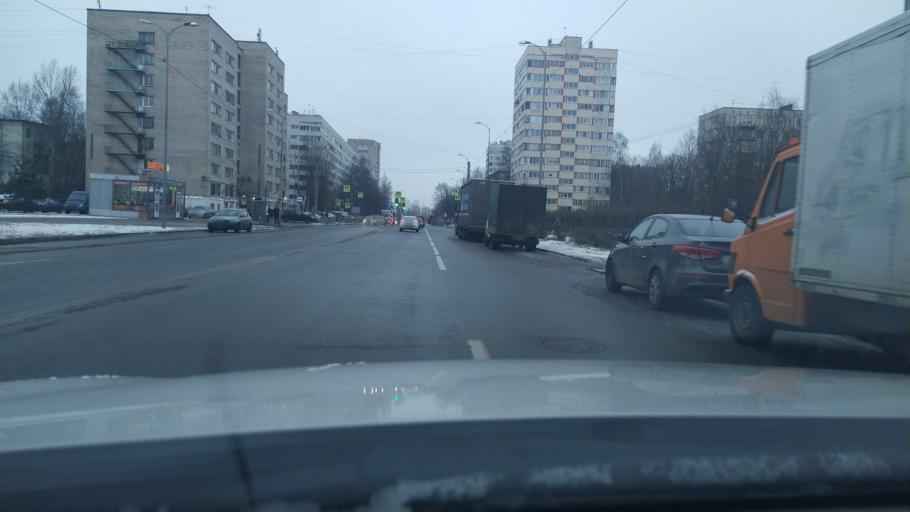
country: RU
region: St.-Petersburg
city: Grazhdanka
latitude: 60.0459
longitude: 30.3894
